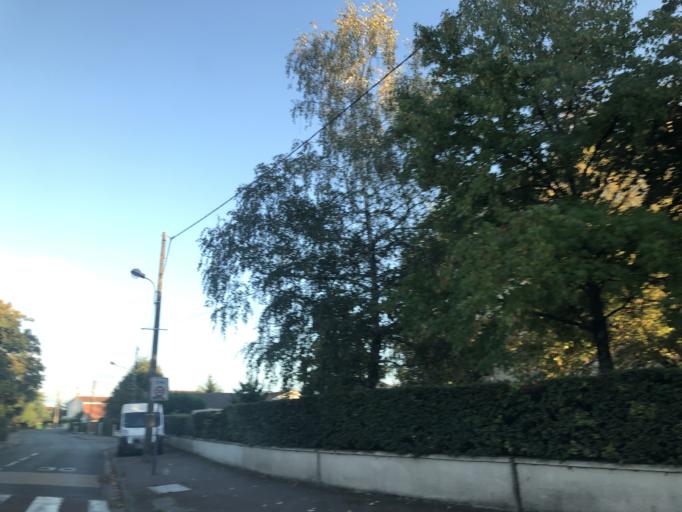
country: FR
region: Aquitaine
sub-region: Departement de la Gironde
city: Merignac
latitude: 44.8426
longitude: -0.6368
